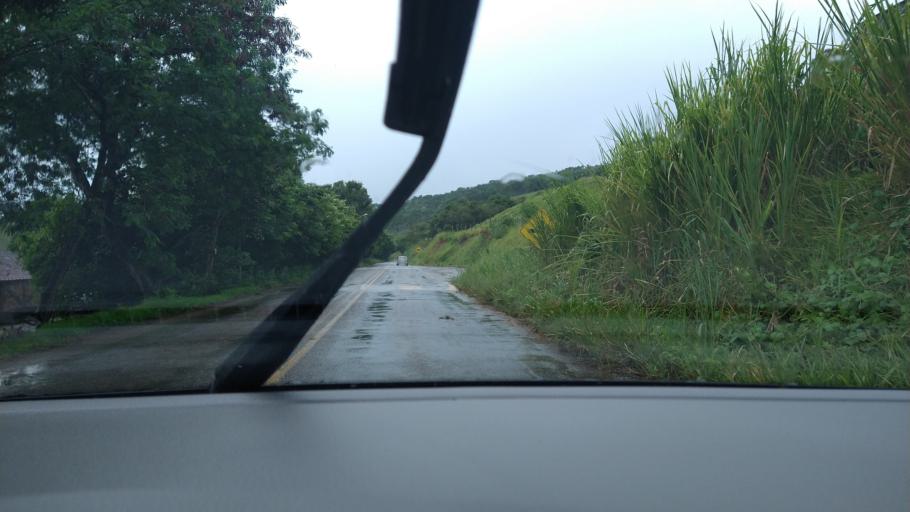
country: BR
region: Minas Gerais
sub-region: Ponte Nova
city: Ponte Nova
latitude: -20.3780
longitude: -42.9008
